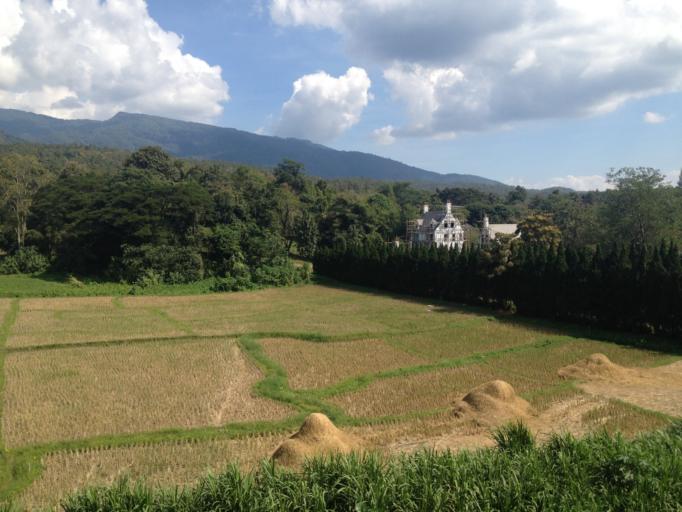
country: TH
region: Chiang Mai
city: Samoeng
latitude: 18.7899
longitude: 98.8387
